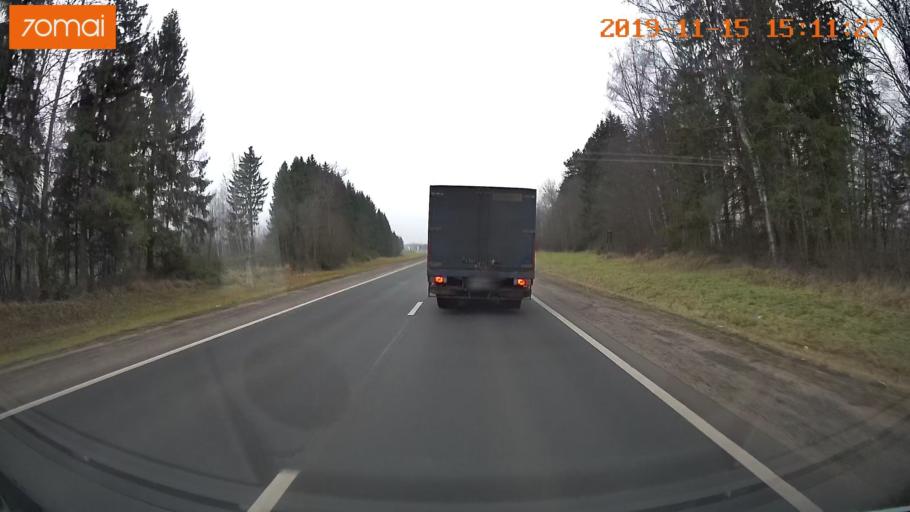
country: RU
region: Jaroslavl
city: Prechistoye
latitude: 58.3363
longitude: 40.2408
